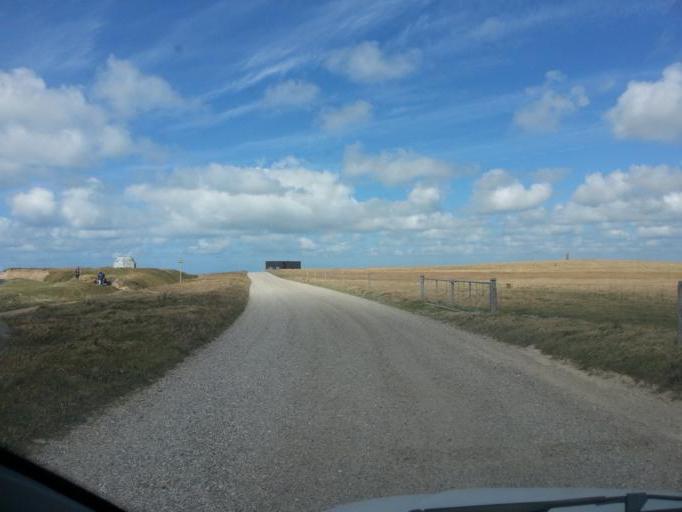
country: DK
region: Central Jutland
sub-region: Lemvig Kommune
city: Harboore
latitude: 56.5138
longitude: 8.1183
